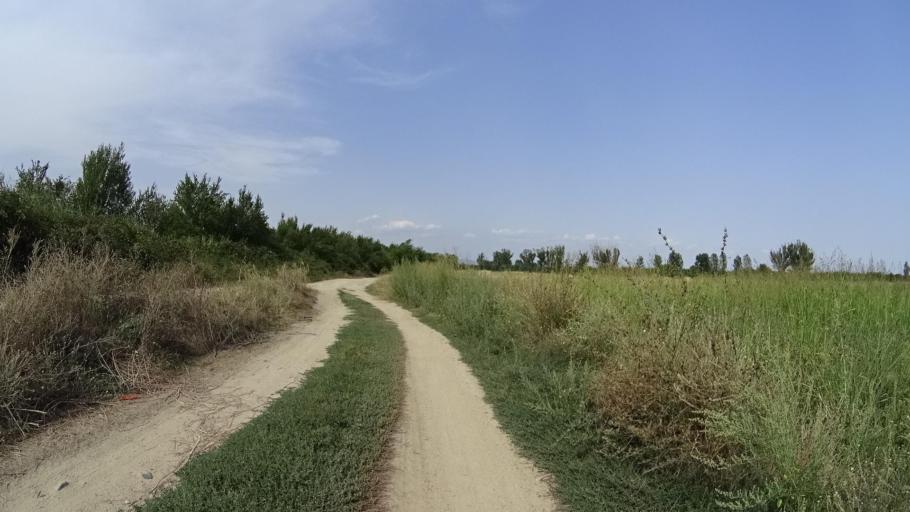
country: BG
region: Plovdiv
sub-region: Obshtina Kaloyanovo
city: Kaloyanovo
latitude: 42.2966
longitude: 24.7965
